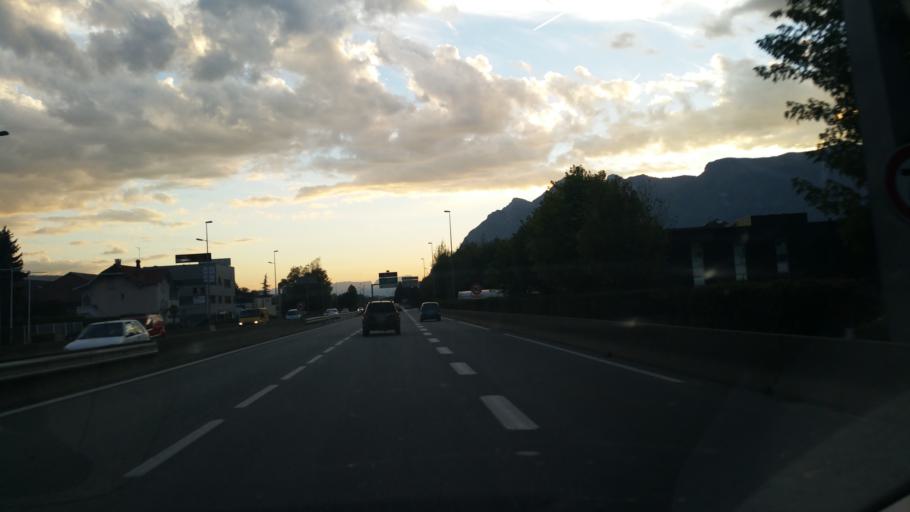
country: FR
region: Rhone-Alpes
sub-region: Departement de la Savoie
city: Grignon
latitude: 45.6605
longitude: 6.3811
